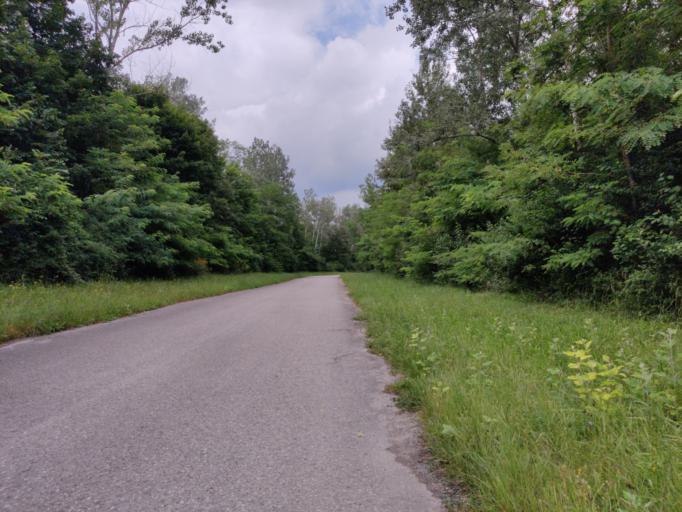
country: AT
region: Lower Austria
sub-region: Politischer Bezirk Melk
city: Melk
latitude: 48.2209
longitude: 15.3097
